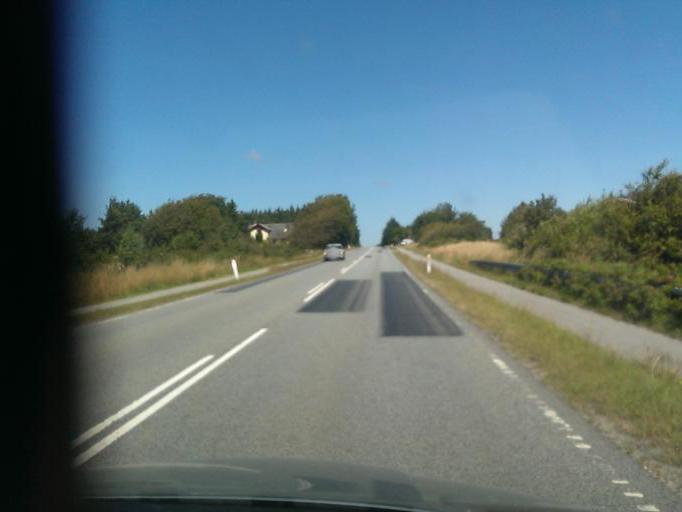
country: DK
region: North Denmark
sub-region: Jammerbugt Kommune
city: Pandrup
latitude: 57.3086
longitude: 9.7027
